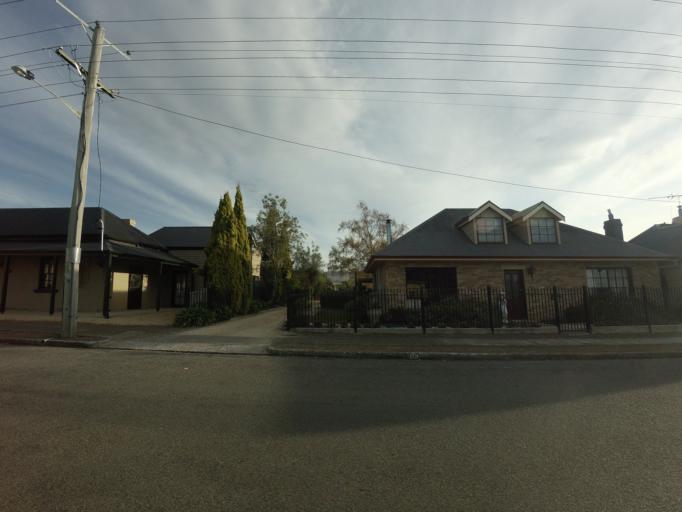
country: AU
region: Tasmania
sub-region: Brighton
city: Bridgewater
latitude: -42.5274
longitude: 147.1980
